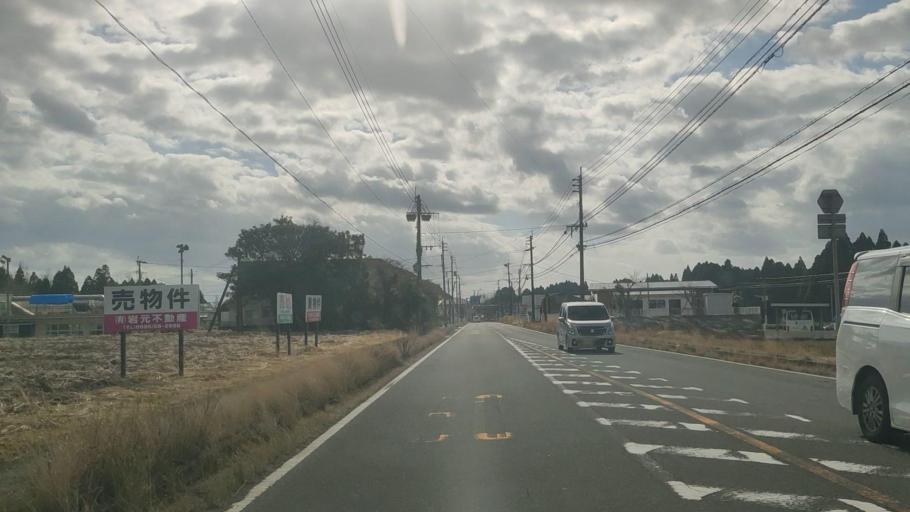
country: JP
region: Kagoshima
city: Kajiki
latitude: 31.7806
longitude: 130.7039
